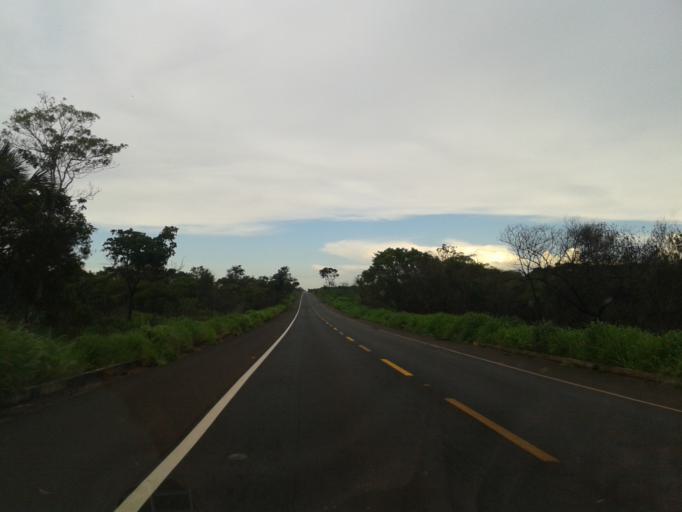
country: BR
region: Minas Gerais
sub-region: Santa Vitoria
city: Santa Vitoria
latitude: -18.9241
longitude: -50.2564
